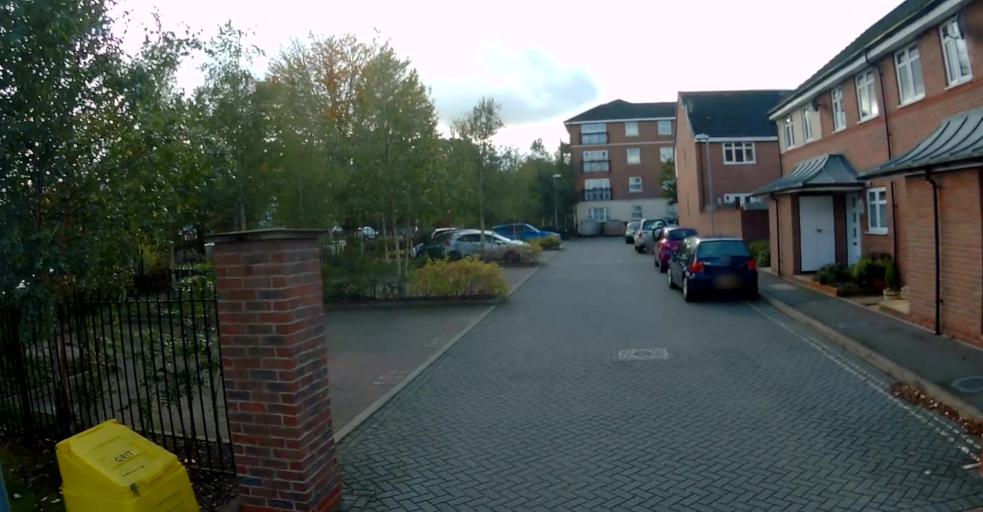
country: GB
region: England
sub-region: Hampshire
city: Farnborough
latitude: 51.2749
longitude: -0.7565
